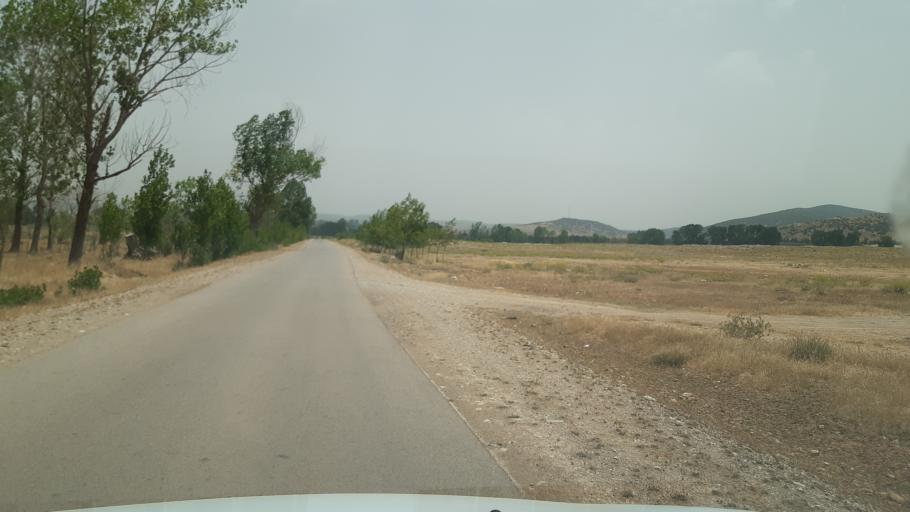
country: MA
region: Meknes-Tafilalet
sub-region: Ifrane
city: Ifrane
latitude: 33.6480
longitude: -5.0275
